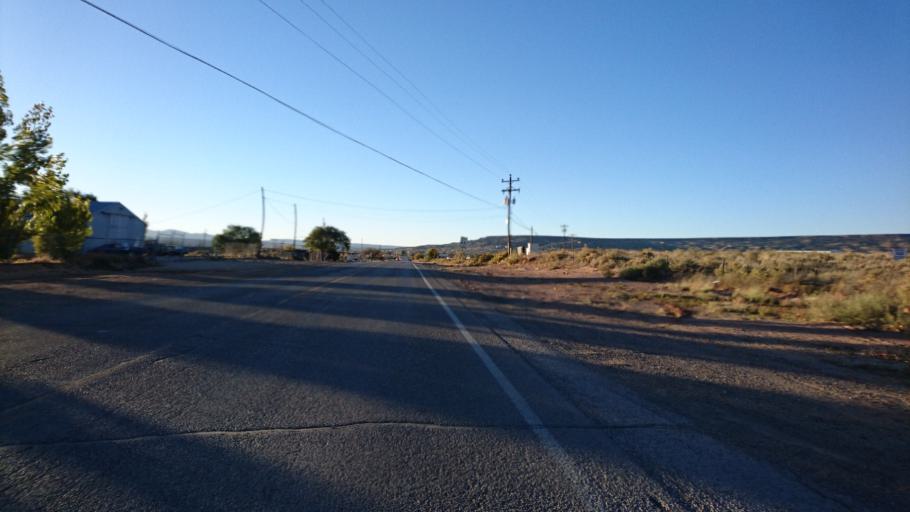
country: US
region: New Mexico
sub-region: Cibola County
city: Grants
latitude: 35.1347
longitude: -107.8186
